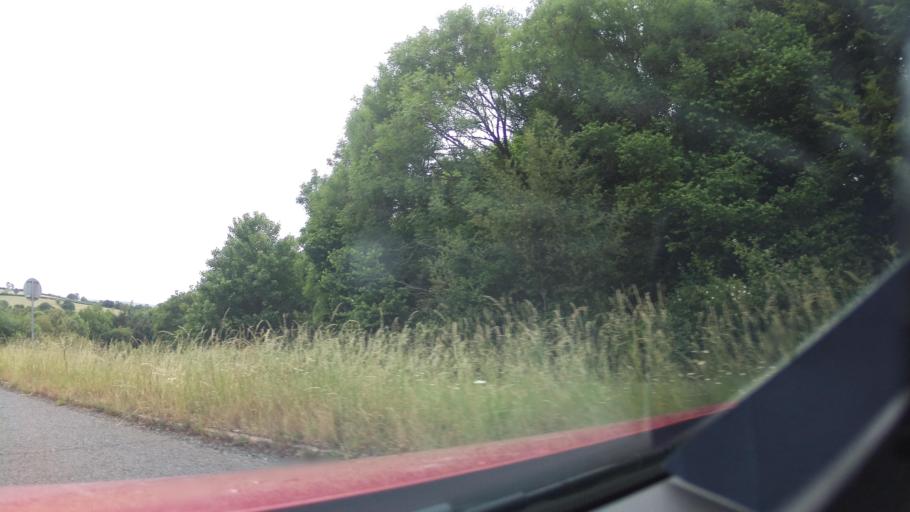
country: GB
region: England
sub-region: Devon
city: Ashburton
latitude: 50.5098
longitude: -3.7614
